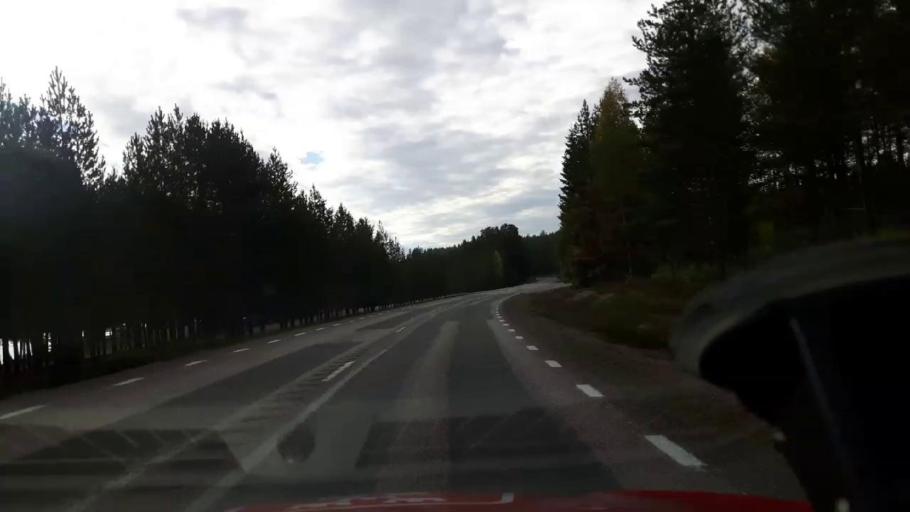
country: SE
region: Gaevleborg
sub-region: Ljusdals Kommun
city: Farila
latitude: 61.9623
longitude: 15.3571
